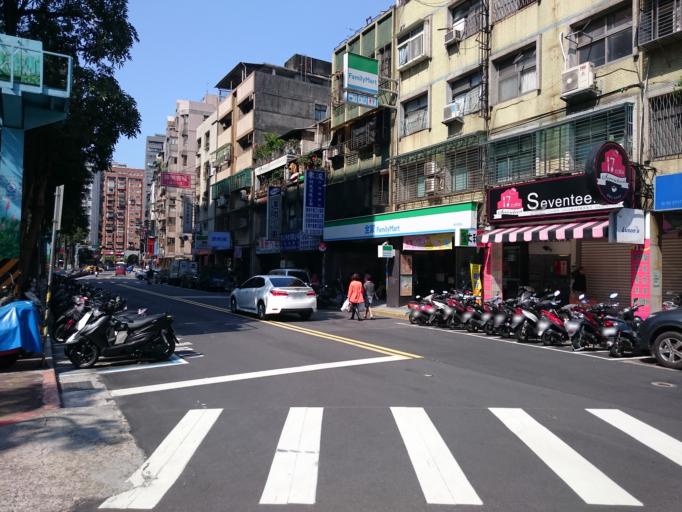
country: TW
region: Taipei
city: Taipei
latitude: 25.0492
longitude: 121.5626
